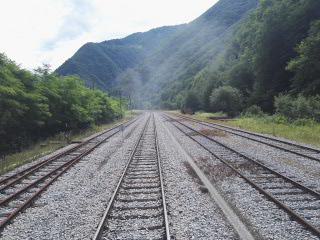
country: SI
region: Tolmin
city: Tolmin
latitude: 46.1516
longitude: 13.8533
